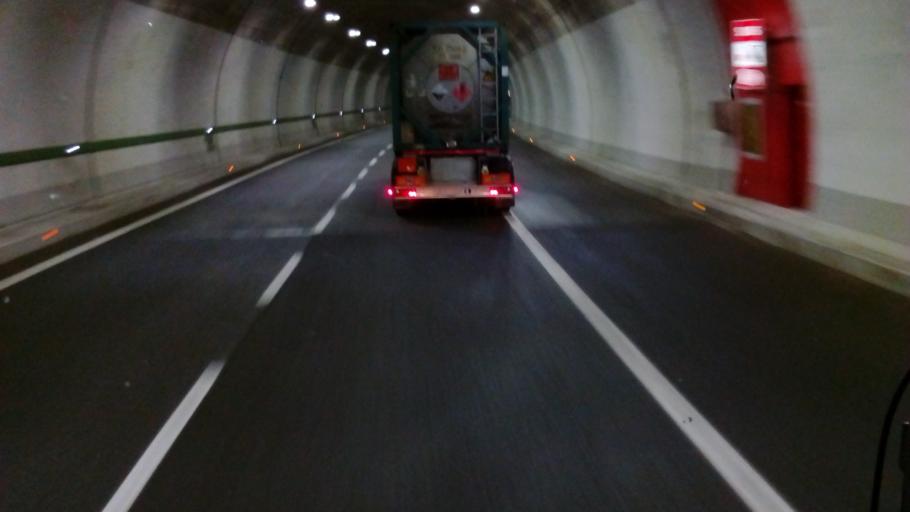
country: IT
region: Tuscany
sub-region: Province of Florence
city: Barberino di Mugello
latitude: 44.0393
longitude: 11.2289
